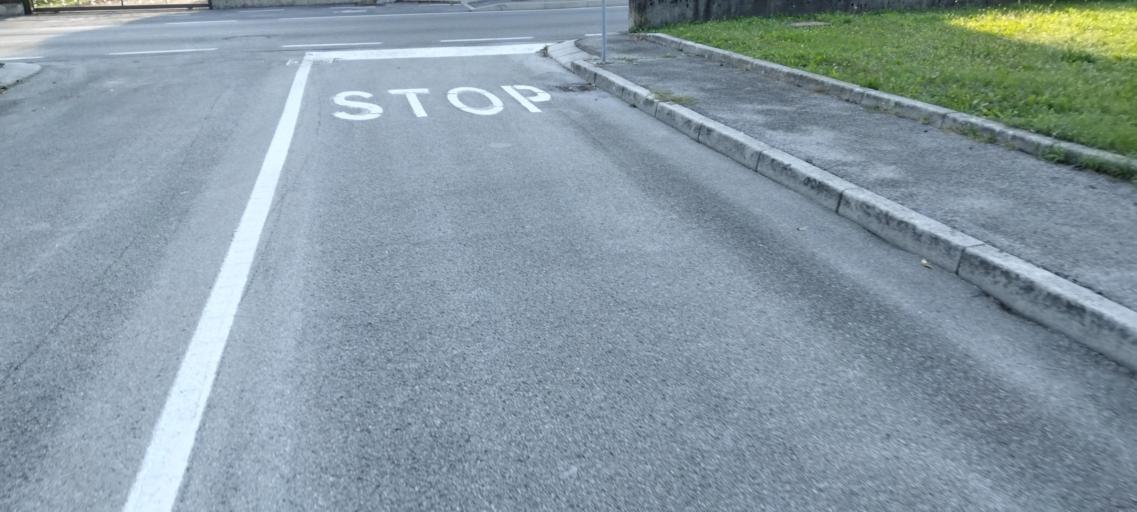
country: IT
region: Veneto
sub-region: Provincia di Vicenza
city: Isola Vicentina
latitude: 45.6311
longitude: 11.4432
